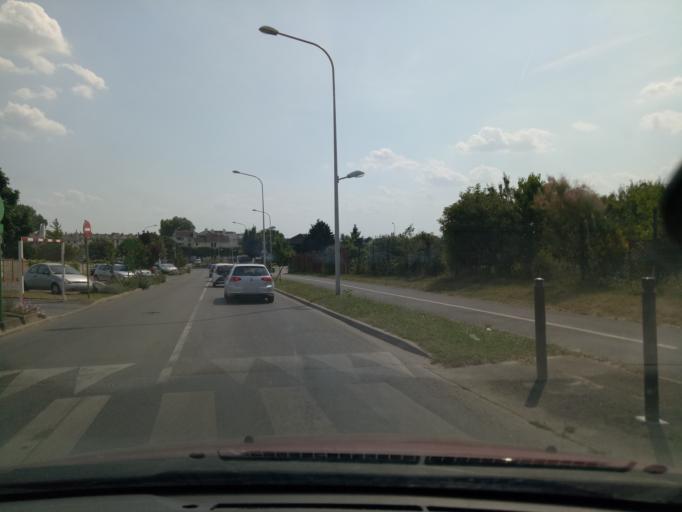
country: FR
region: Ile-de-France
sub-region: Departement des Yvelines
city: Montesson
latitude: 48.9132
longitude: 2.1472
